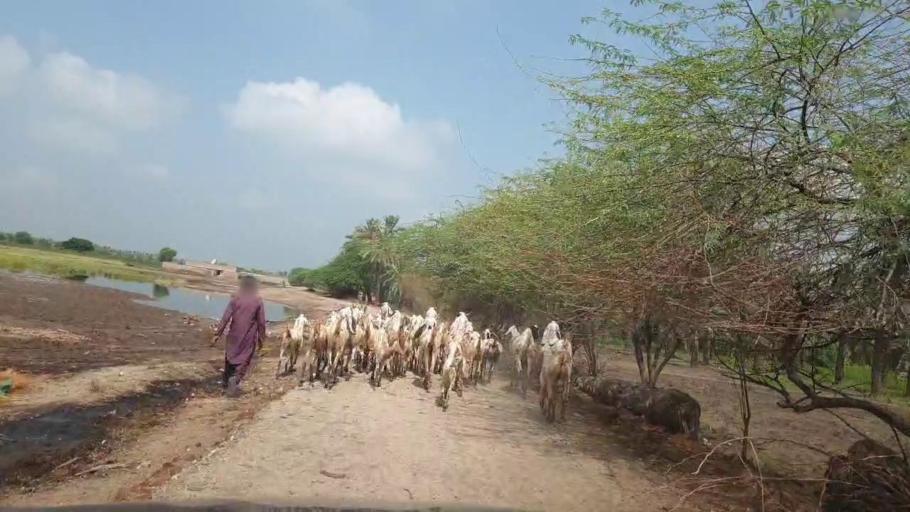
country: PK
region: Sindh
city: Pir jo Goth
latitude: 27.6044
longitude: 68.7005
